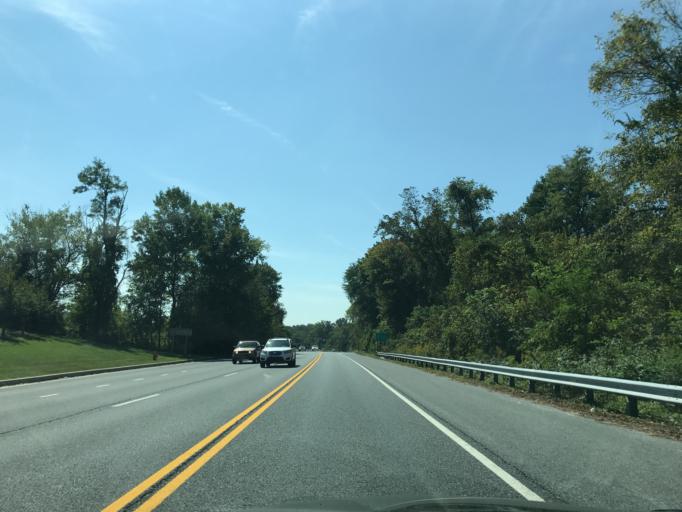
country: US
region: Maryland
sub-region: Anne Arundel County
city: Jessup
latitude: 39.1912
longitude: -76.7956
